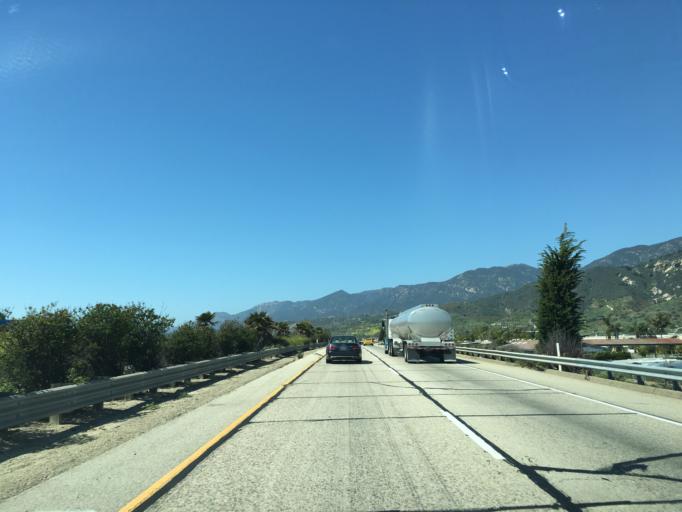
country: US
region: California
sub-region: Santa Barbara County
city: Toro Canyon
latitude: 34.4099
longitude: -119.5515
